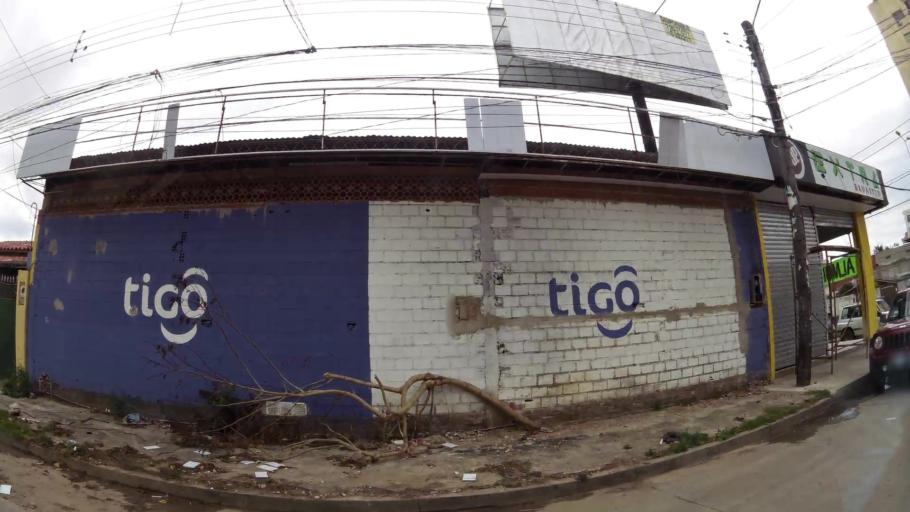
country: BO
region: Santa Cruz
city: Santa Cruz de la Sierra
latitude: -17.7696
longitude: -63.2020
